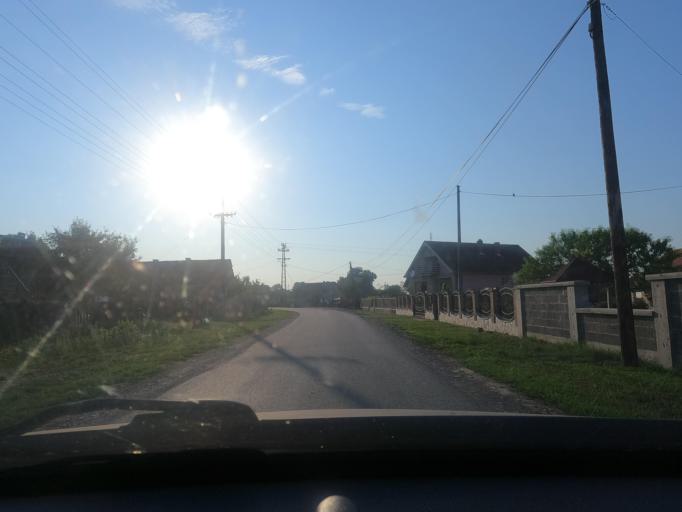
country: RS
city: Bogosavac
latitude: 44.7525
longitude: 19.5762
